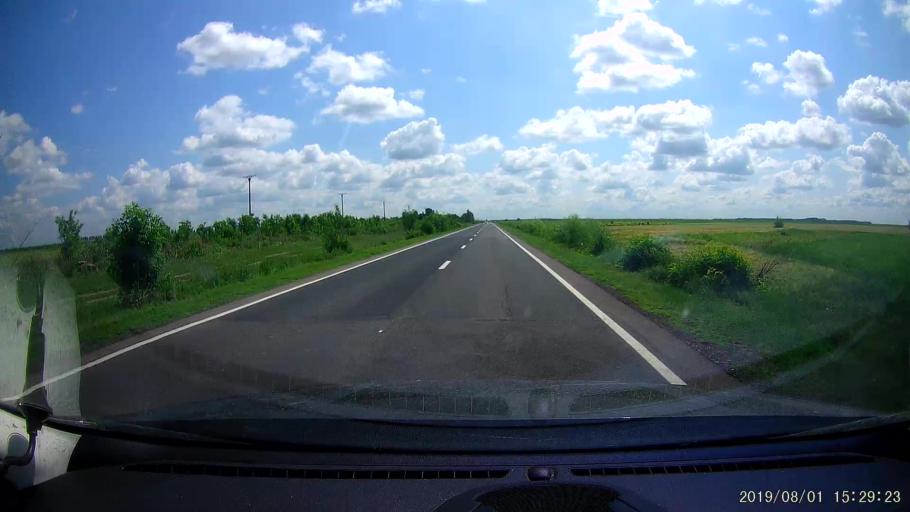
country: RO
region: Braila
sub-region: Comuna Viziru
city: Viziru
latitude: 44.9828
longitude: 27.6977
